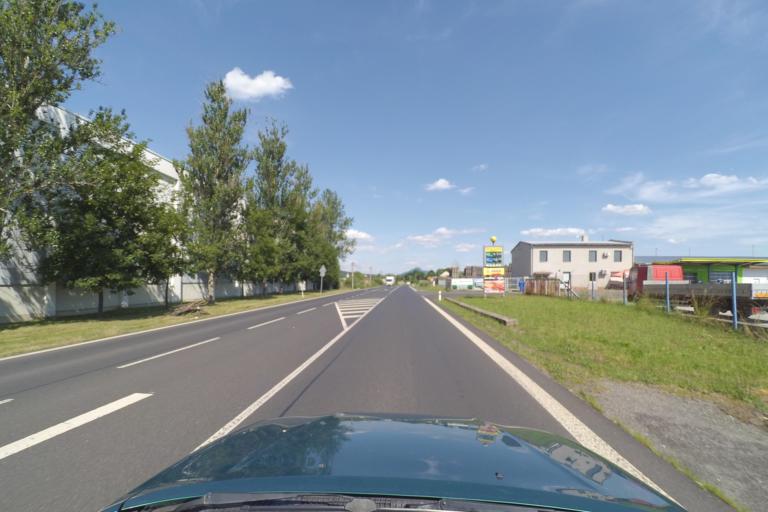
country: CZ
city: Zakupy
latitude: 50.6815
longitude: 14.6292
